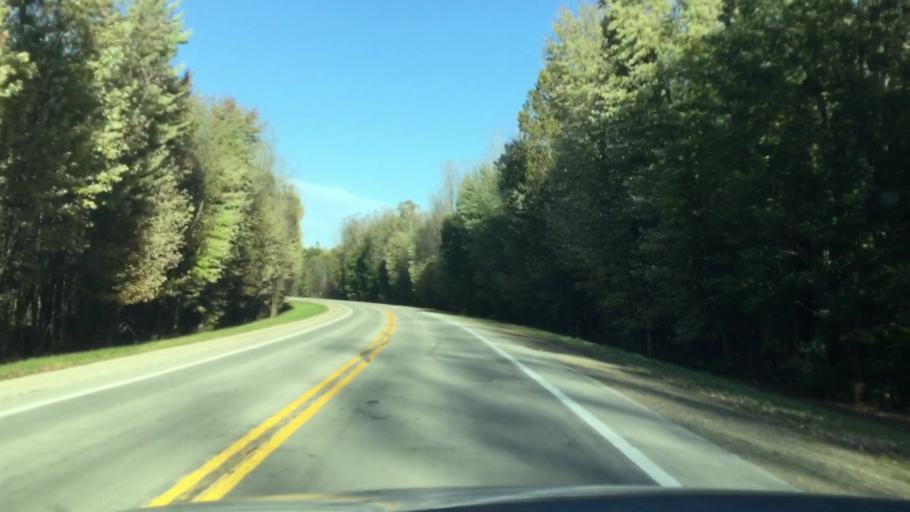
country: US
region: Michigan
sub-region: Lapeer County
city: Barnes Lake-Millers Lake
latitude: 43.2202
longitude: -83.3072
